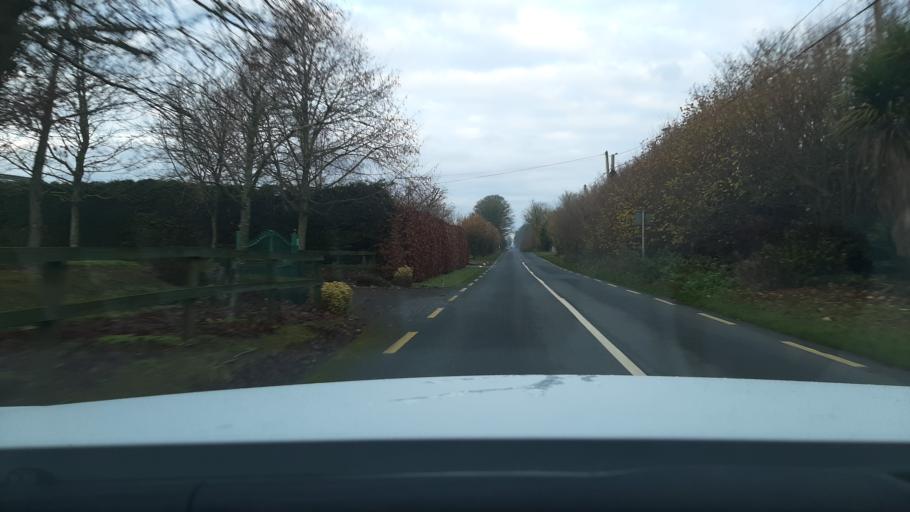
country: IE
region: Leinster
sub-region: Kildare
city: Rathangan
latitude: 53.2356
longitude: -7.0102
